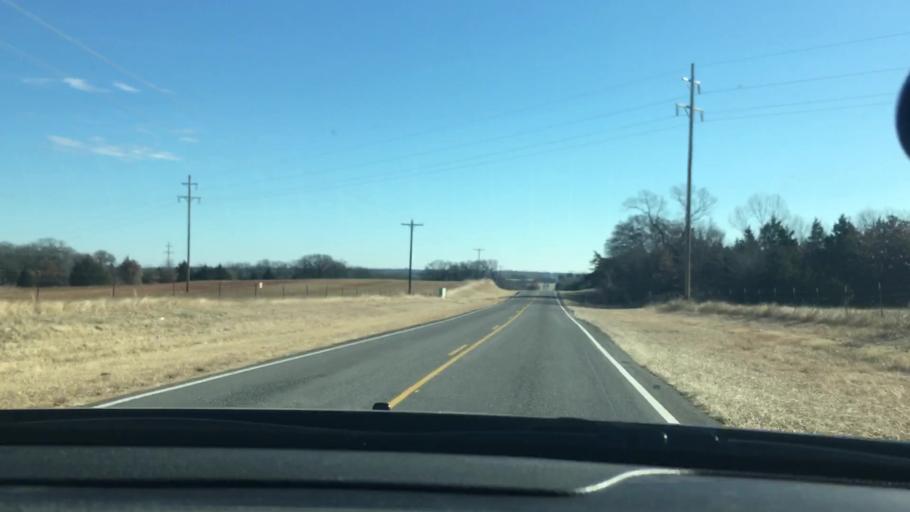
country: US
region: Oklahoma
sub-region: Love County
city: Marietta
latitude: 33.9403
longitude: -97.3340
